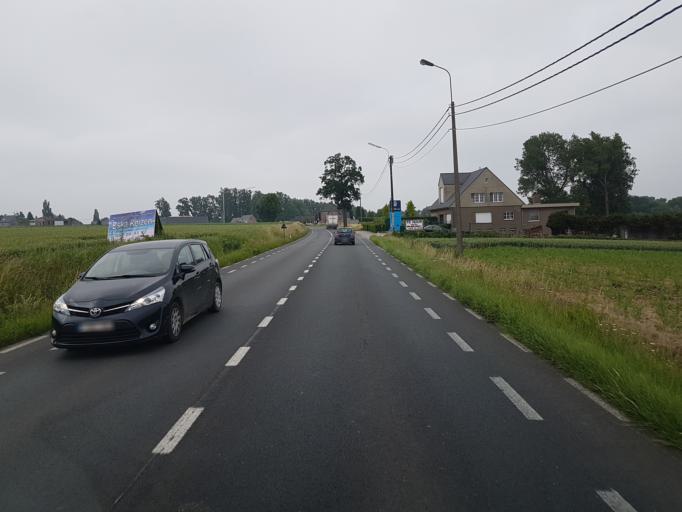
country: BE
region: Flanders
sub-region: Provincie Oost-Vlaanderen
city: Perre
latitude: 50.8555
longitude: 3.8571
